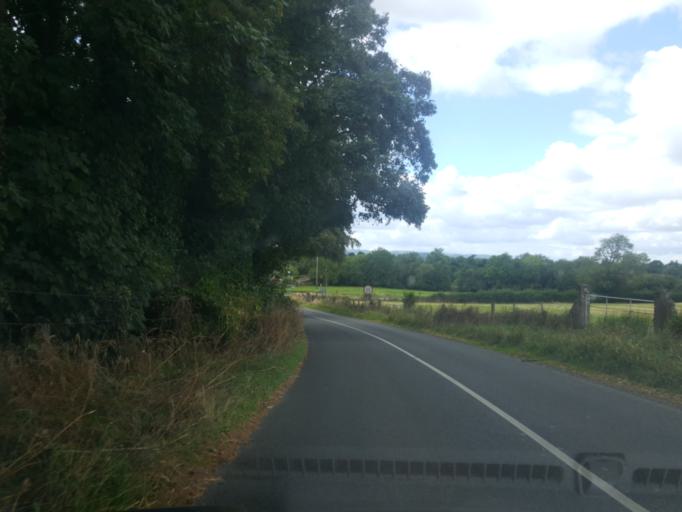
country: IE
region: Leinster
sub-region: County Carlow
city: Carlow
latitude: 52.9088
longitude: -6.9304
